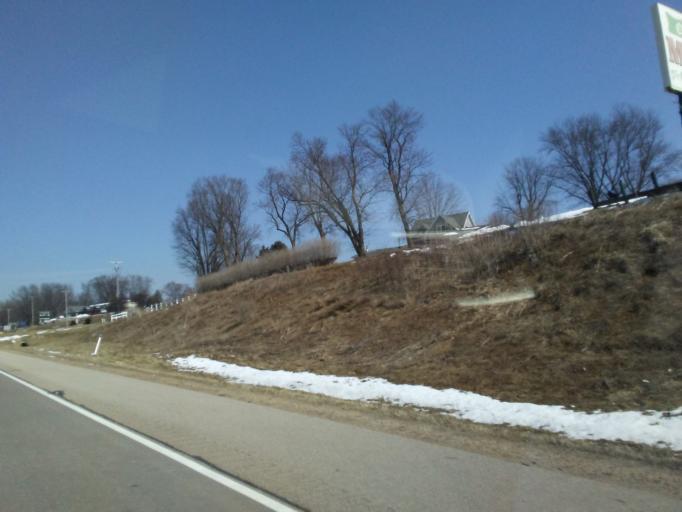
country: US
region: Wisconsin
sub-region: Vernon County
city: Westby
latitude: 43.6400
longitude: -90.8660
